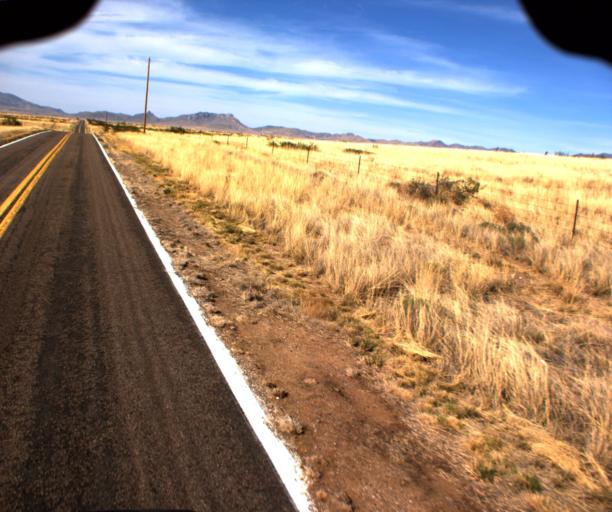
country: US
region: Arizona
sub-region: Cochise County
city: Willcox
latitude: 31.9548
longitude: -109.4772
